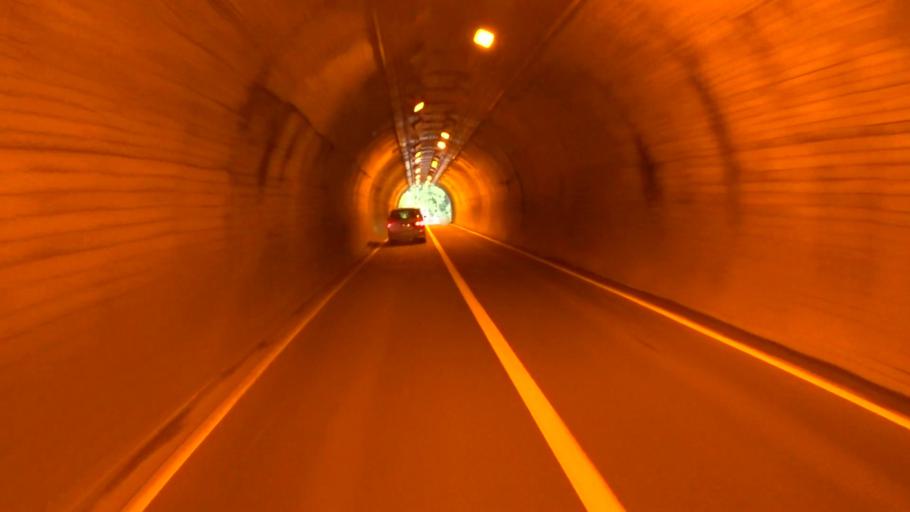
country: JP
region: Kyoto
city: Uji
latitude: 34.9124
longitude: 135.7497
